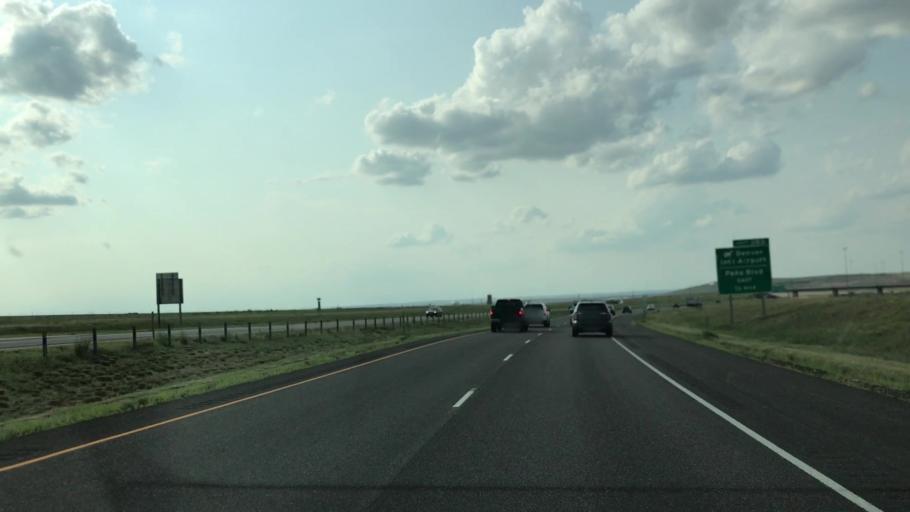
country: US
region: Colorado
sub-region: Adams County
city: Aurora
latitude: 39.8214
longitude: -104.7435
